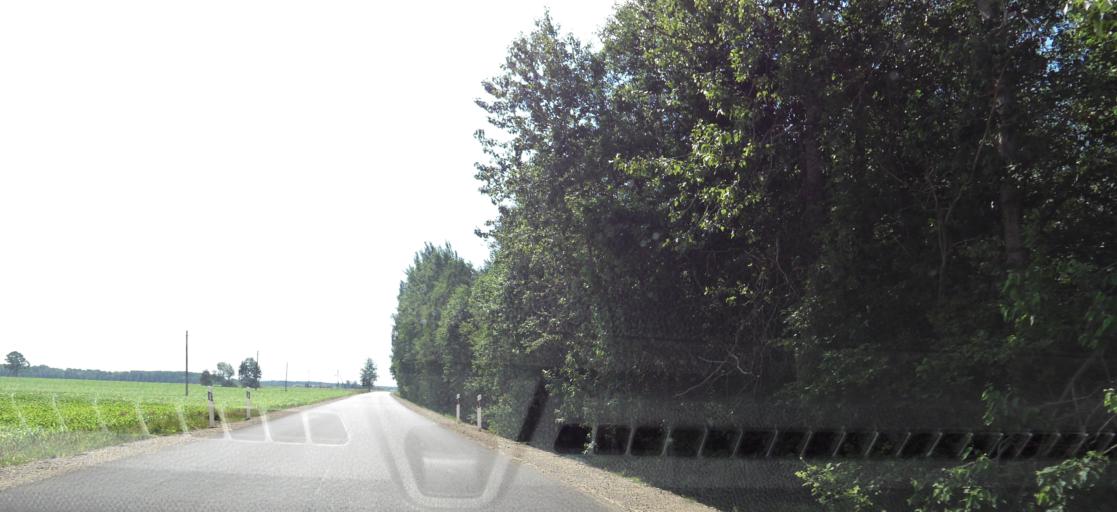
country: LT
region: Panevezys
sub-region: Birzai
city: Birzai
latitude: 56.2096
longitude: 24.9092
